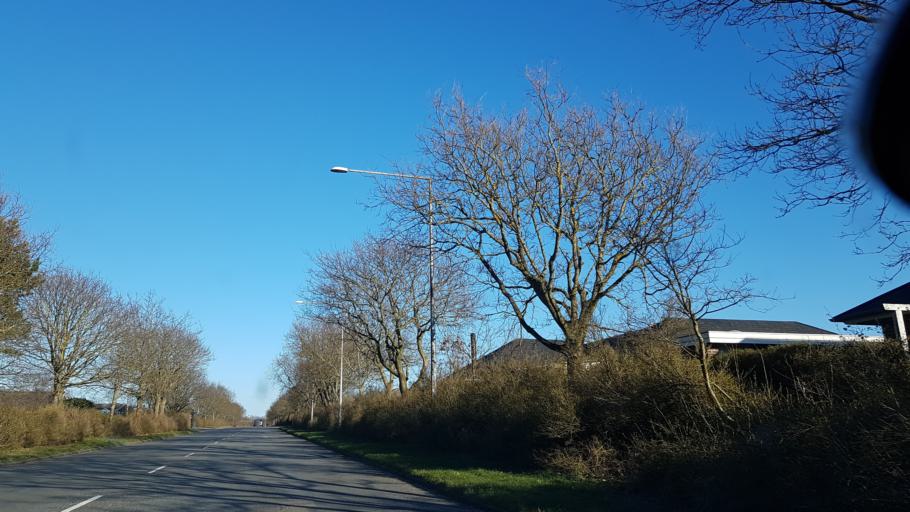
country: DK
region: South Denmark
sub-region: Fano Kommune
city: Nordby
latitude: 55.5117
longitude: 8.3972
